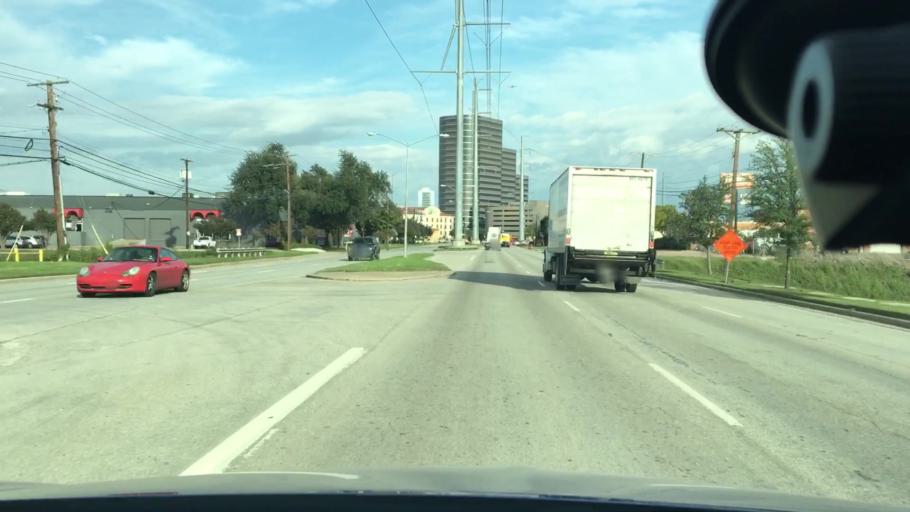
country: US
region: Texas
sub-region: Dallas County
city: Dallas
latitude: 32.8088
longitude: -96.8559
